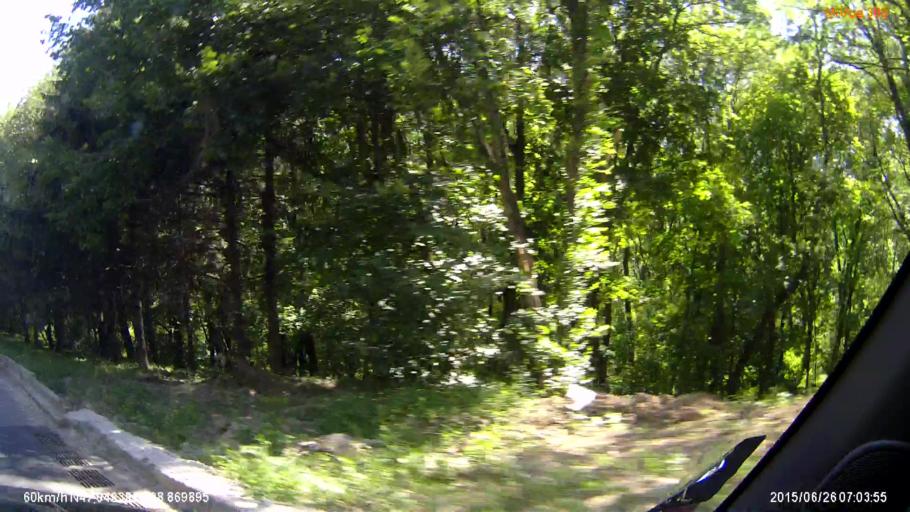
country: MD
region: Chisinau
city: Chisinau
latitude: 47.0462
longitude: 28.8698
